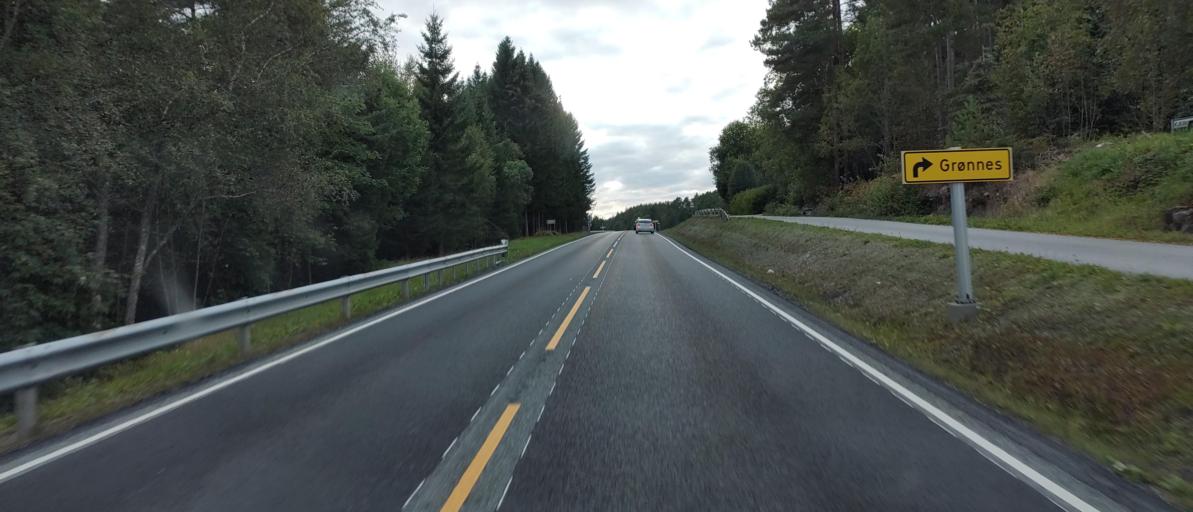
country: NO
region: More og Romsdal
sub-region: Molde
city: Hjelset
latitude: 62.7334
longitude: 7.3996
